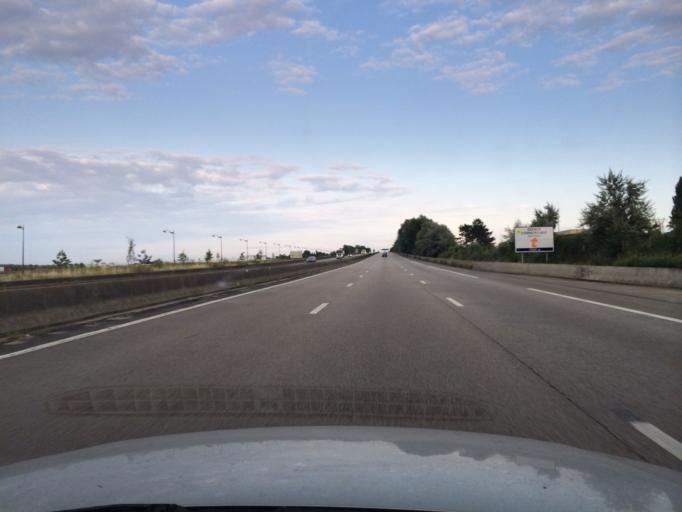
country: FR
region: Ile-de-France
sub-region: Departement des Yvelines
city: Buchelay
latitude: 48.9874
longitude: 1.6617
